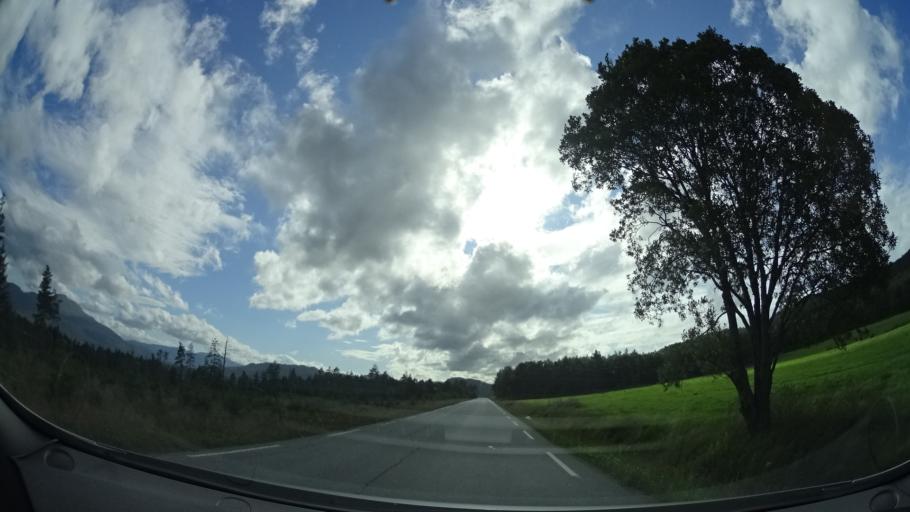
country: NO
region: More og Romsdal
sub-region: Halsa
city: Liaboen
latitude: 63.1231
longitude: 8.3339
